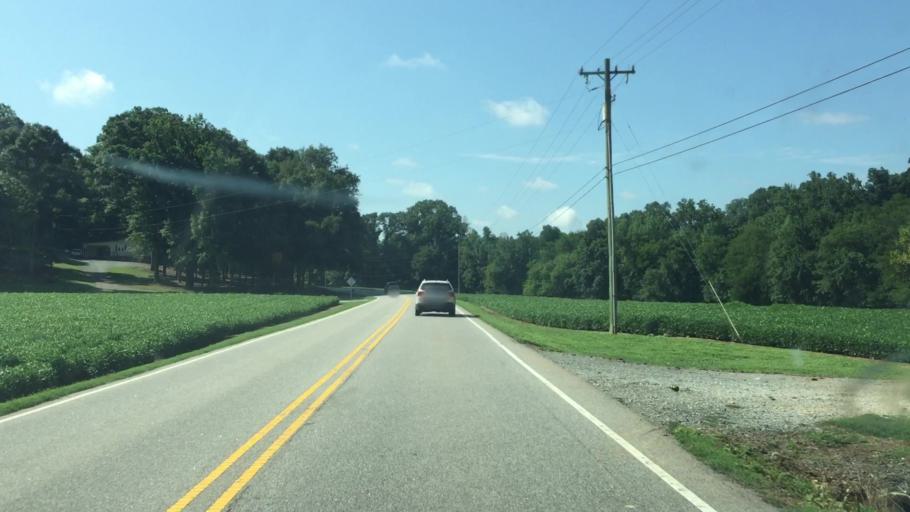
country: US
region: North Carolina
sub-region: Anson County
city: Burnsville
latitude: 35.1129
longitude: -80.3374
